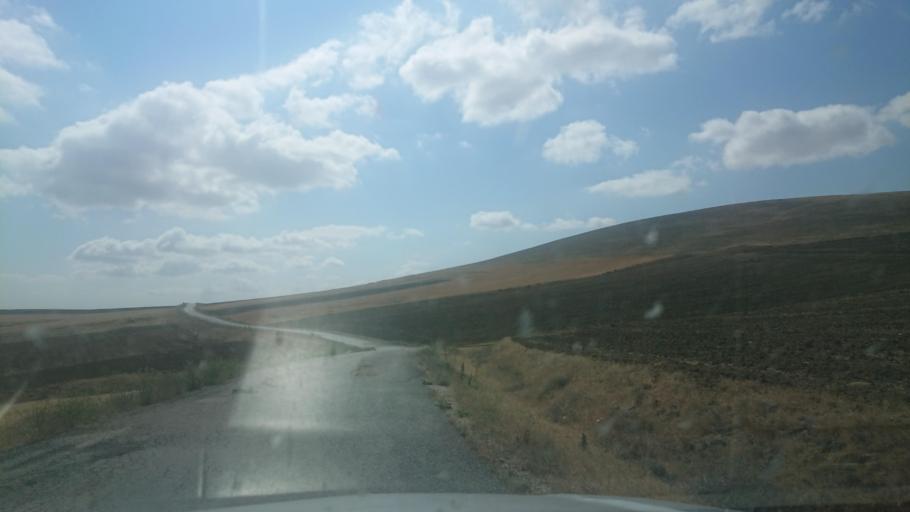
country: TR
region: Aksaray
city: Sariyahsi
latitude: 39.0032
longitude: 33.9638
